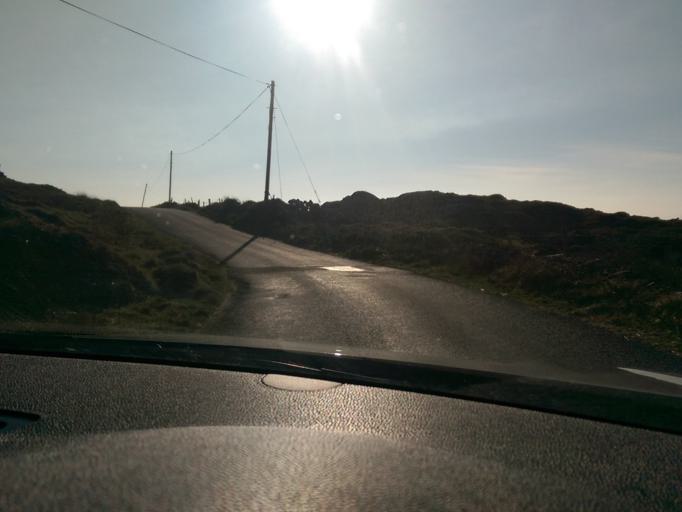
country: IE
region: Connaught
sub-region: County Galway
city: Clifden
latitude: 53.3659
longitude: -9.8742
